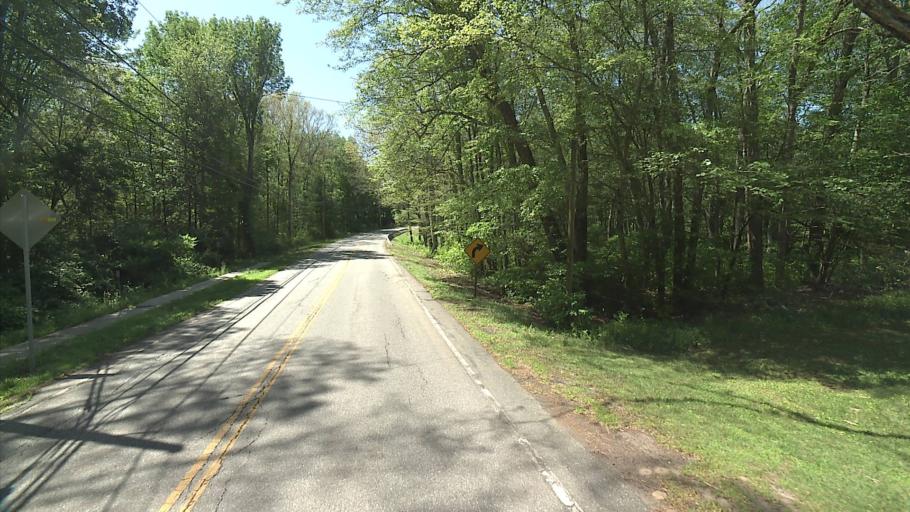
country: US
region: Connecticut
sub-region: New London County
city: Colchester
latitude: 41.5917
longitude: -72.3042
